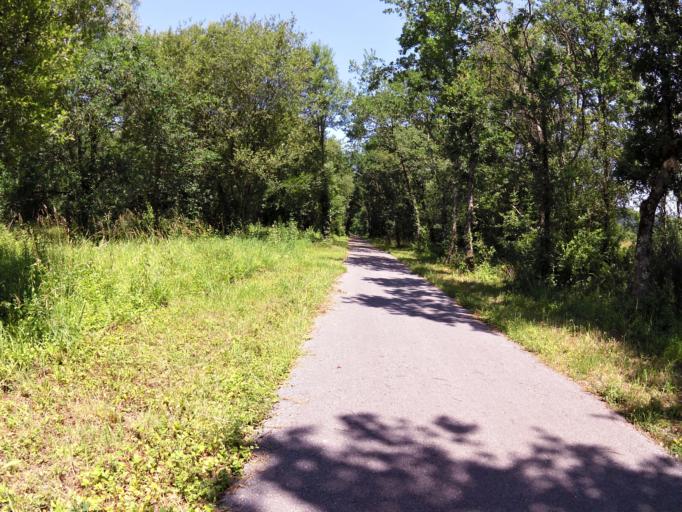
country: FR
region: Aquitaine
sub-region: Departement des Pyrenees-Atlantiques
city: Sauveterre-de-Bearn
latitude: 43.4422
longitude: -0.9948
